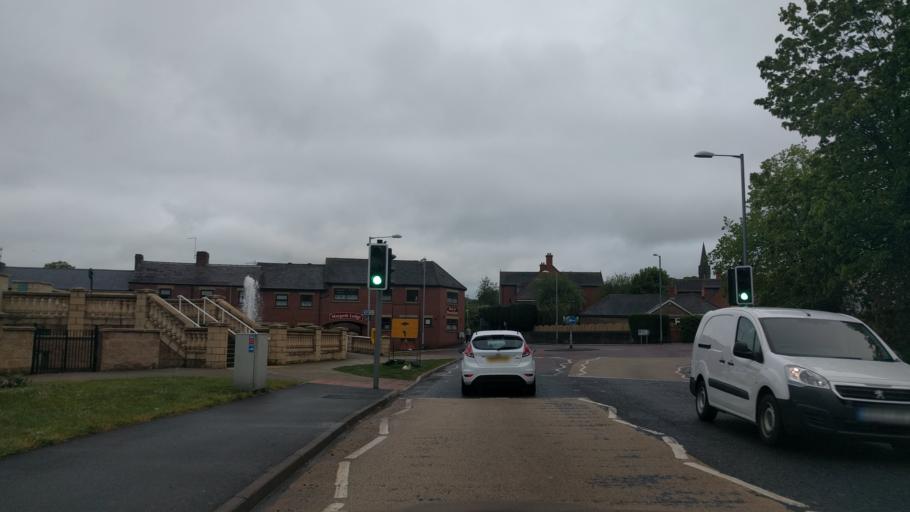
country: GB
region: England
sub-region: Northumberland
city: Morpeth
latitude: 55.1688
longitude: -1.6858
